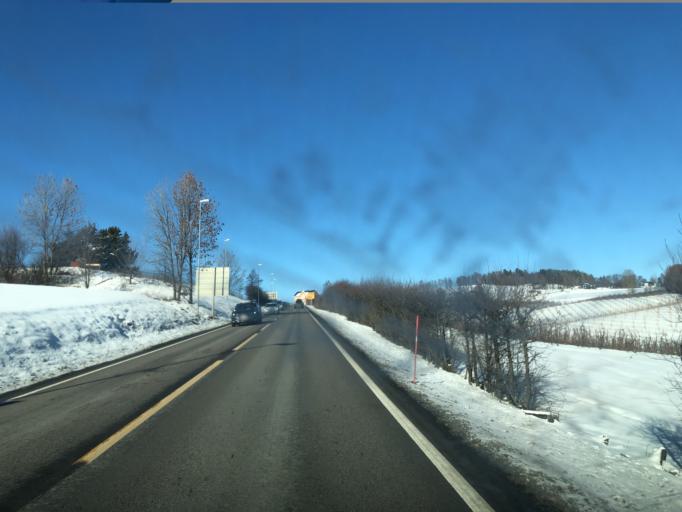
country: NO
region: Buskerud
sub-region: Ringerike
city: Honefoss
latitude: 60.1318
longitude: 10.2743
